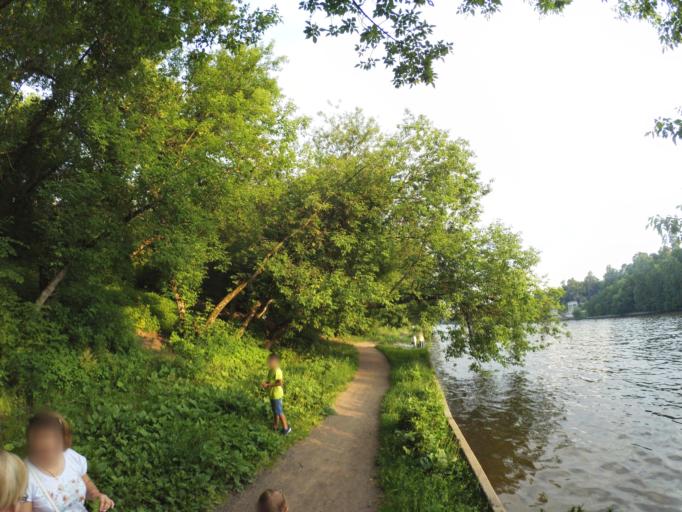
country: RU
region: Moscow
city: Shchukino
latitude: 55.7870
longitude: 37.4465
